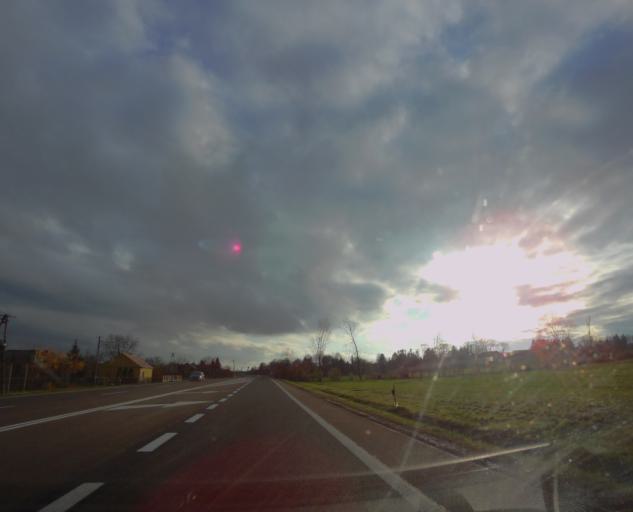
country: PL
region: Subcarpathian Voivodeship
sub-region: Powiat przemyski
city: Orly
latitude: 49.9030
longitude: 22.8170
